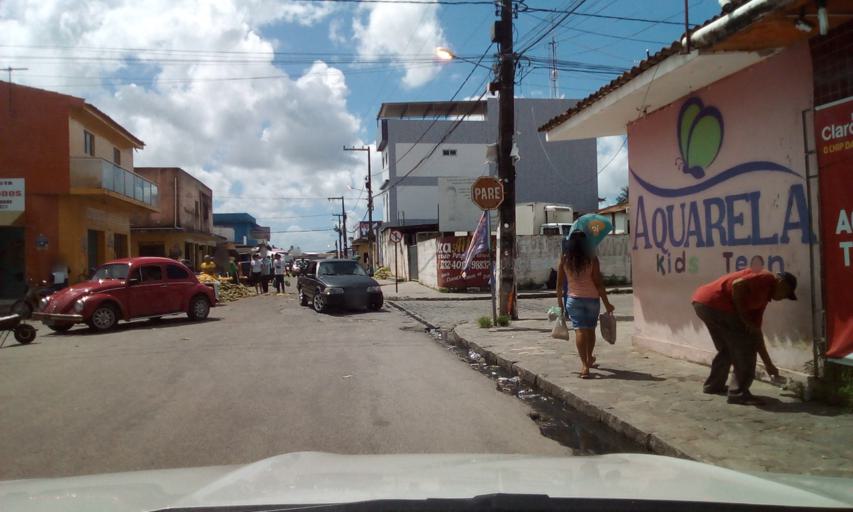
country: BR
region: Paraiba
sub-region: Bayeux
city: Bayeux
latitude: -7.1324
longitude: -34.9274
